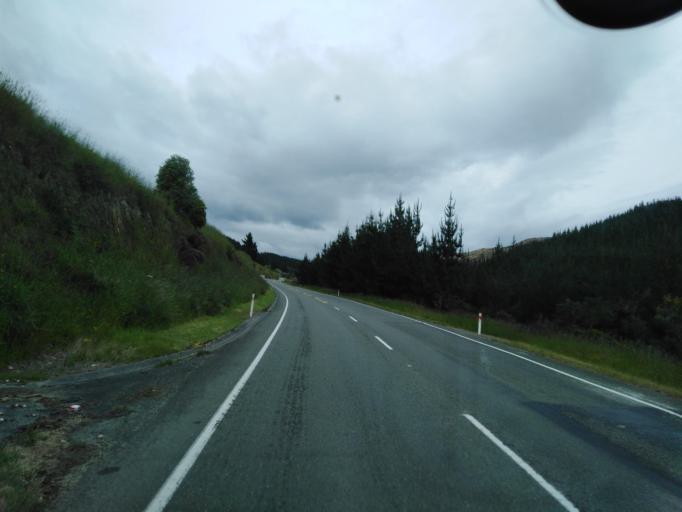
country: NZ
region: Tasman
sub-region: Tasman District
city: Wakefield
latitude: -41.4636
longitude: 172.9483
